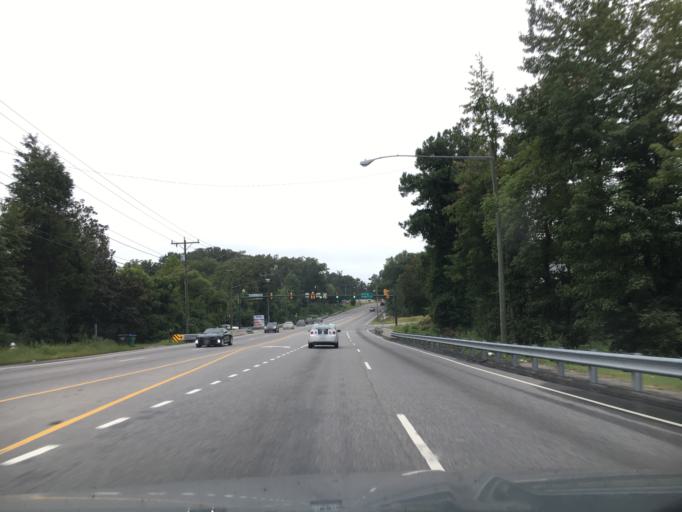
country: US
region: Virginia
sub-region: Chesterfield County
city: Bon Air
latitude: 37.4830
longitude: -77.5031
